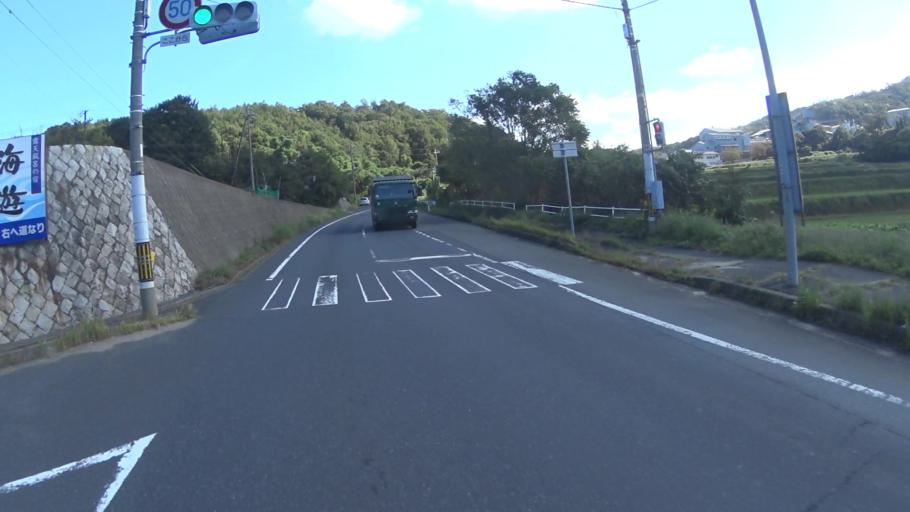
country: JP
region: Kyoto
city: Miyazu
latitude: 35.7011
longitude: 135.0624
